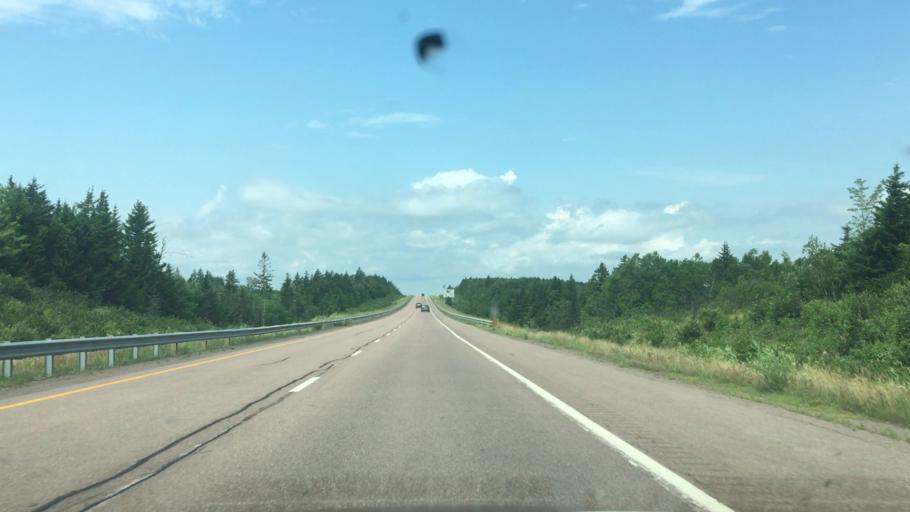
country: CA
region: New Brunswick
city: Sackville
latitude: 45.9522
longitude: -64.4072
